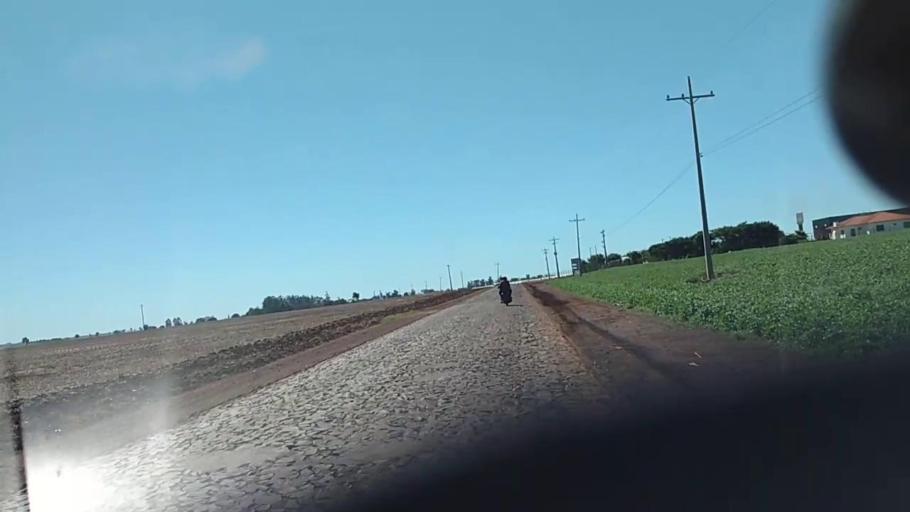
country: PY
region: Alto Parana
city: Naranjal
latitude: -25.9714
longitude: -55.1519
